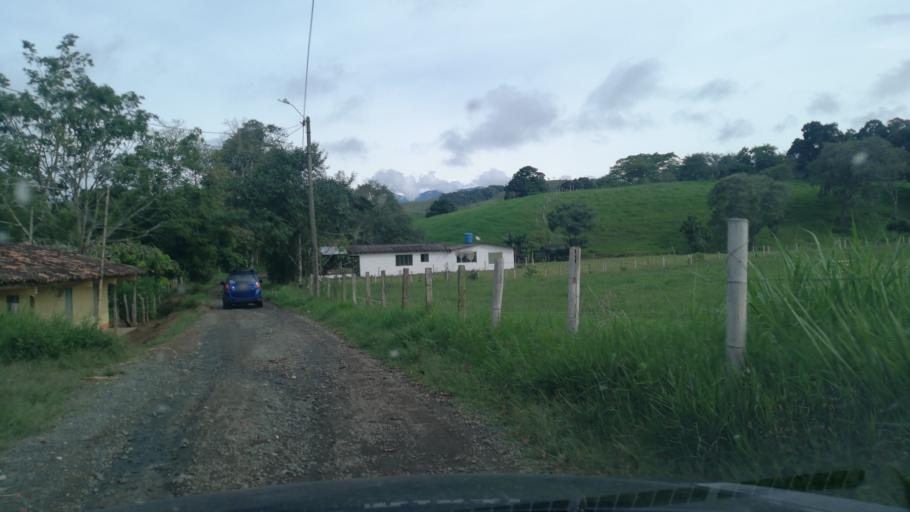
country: CO
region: Valle del Cauca
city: Restrepo
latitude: 3.8523
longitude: -76.4588
